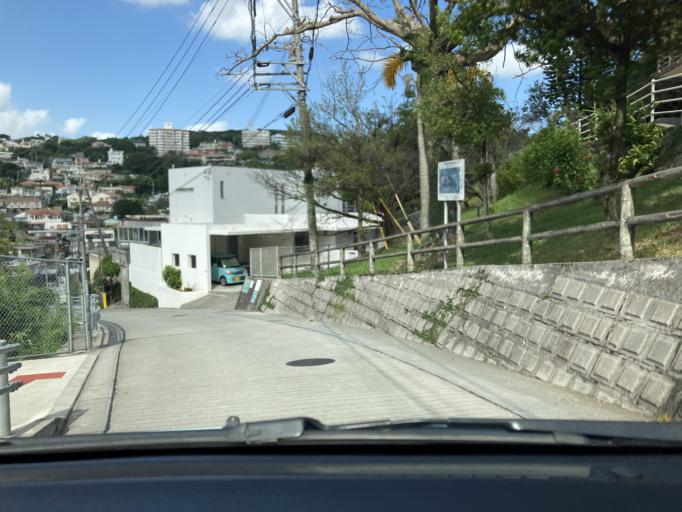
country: JP
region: Okinawa
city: Naha-shi
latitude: 26.2126
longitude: 127.7134
